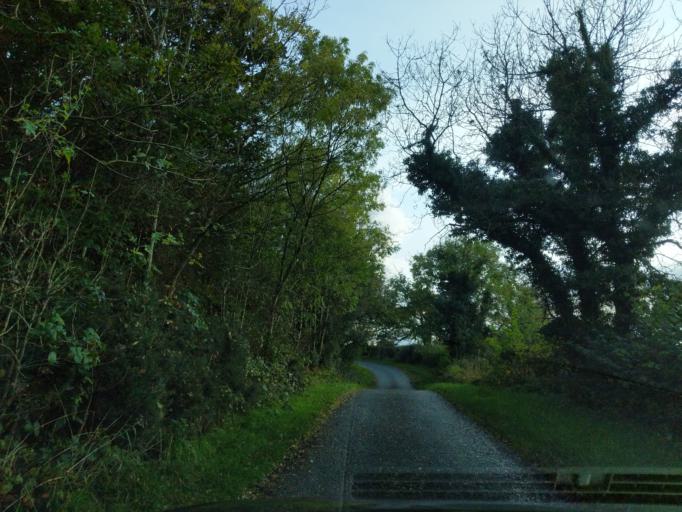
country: GB
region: Scotland
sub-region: Dumfries and Galloway
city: Kirkcudbright
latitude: 54.8403
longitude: -4.1801
